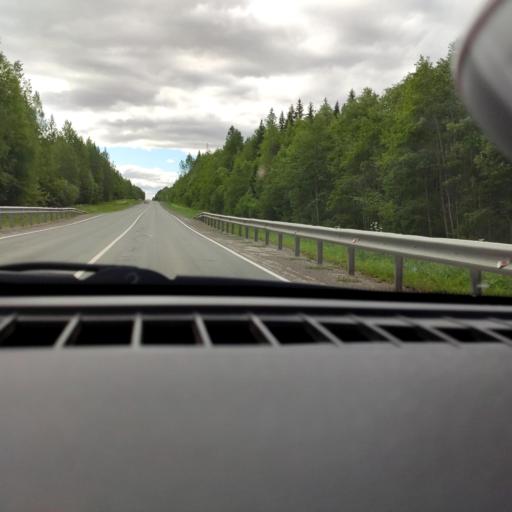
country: RU
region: Perm
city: Perm
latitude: 58.1625
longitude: 56.2436
